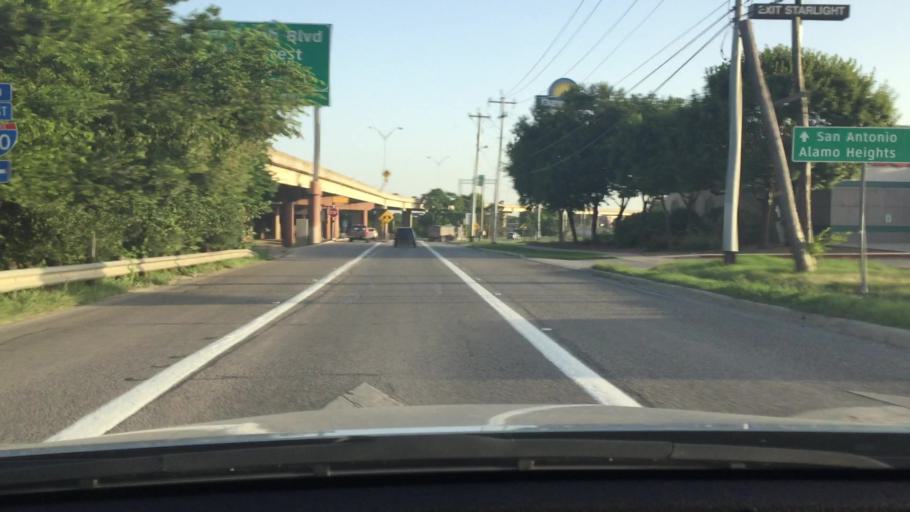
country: US
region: Texas
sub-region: Bexar County
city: Windcrest
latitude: 29.5245
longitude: -98.3941
